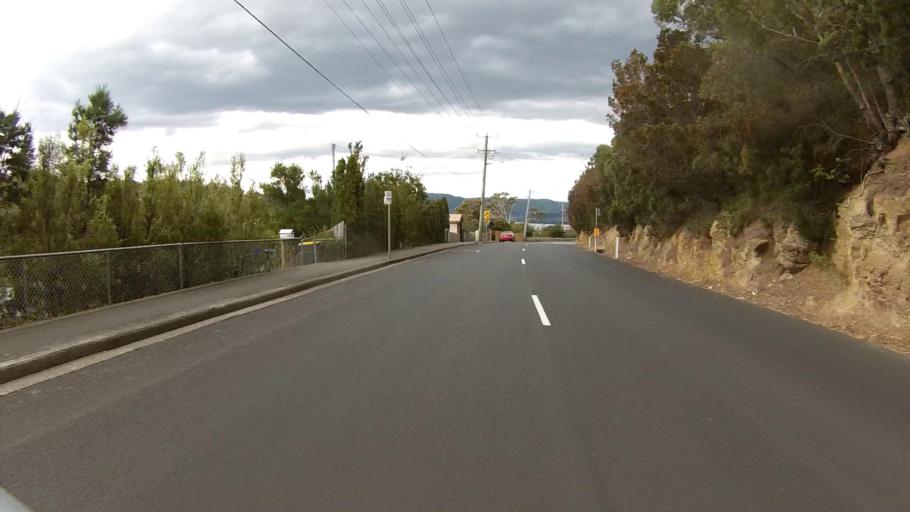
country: AU
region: Tasmania
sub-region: Hobart
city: Dynnyrne
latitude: -42.8988
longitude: 147.3004
